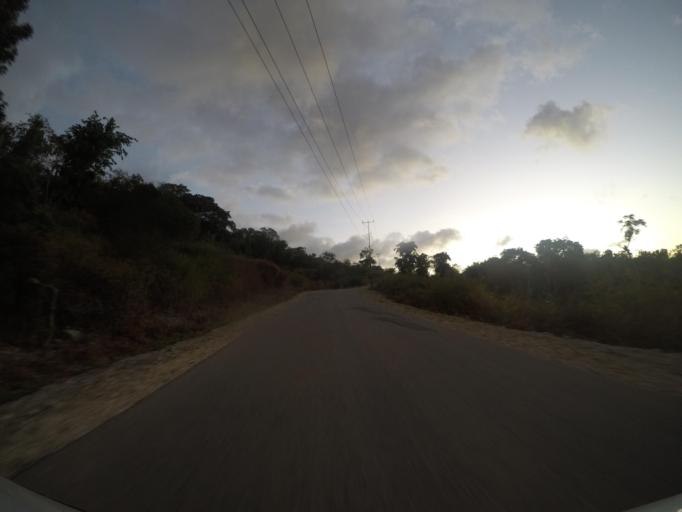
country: TL
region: Lautem
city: Lospalos
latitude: -8.3643
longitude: 127.0479
